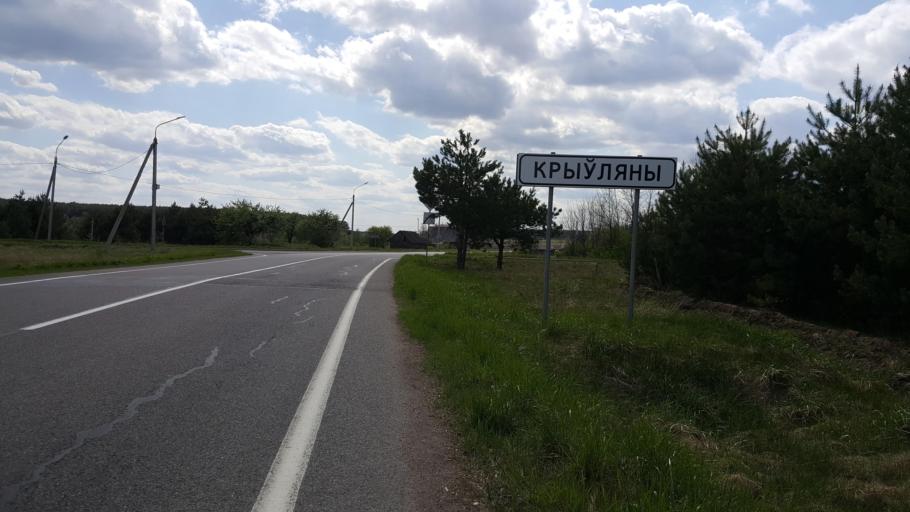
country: BY
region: Brest
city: Kamyanyets
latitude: 52.3949
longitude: 23.9857
